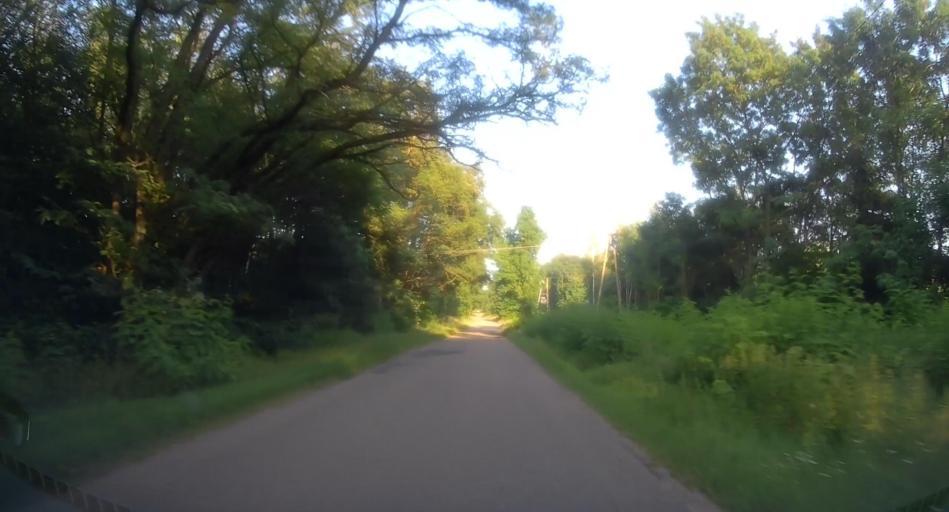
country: PL
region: Lodz Voivodeship
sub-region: Powiat skierniewicki
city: Kowiesy
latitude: 51.9037
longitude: 20.3592
